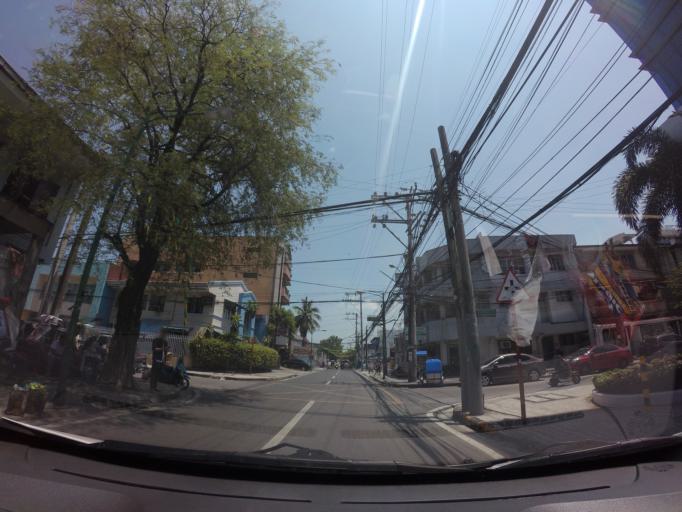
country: PH
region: Metro Manila
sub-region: Makati City
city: Makati City
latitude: 14.5593
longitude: 121.0031
